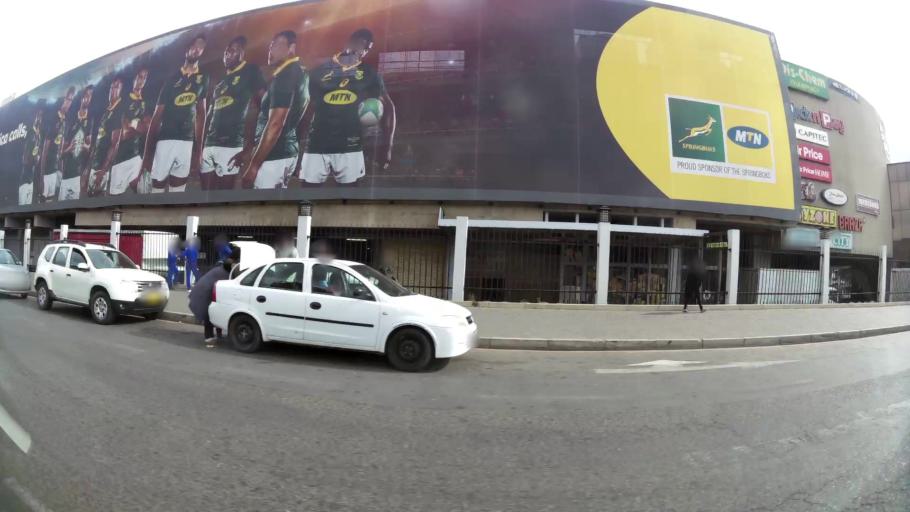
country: ZA
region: Orange Free State
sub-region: Mangaung Metropolitan Municipality
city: Bloemfontein
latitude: -29.1144
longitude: 26.2117
